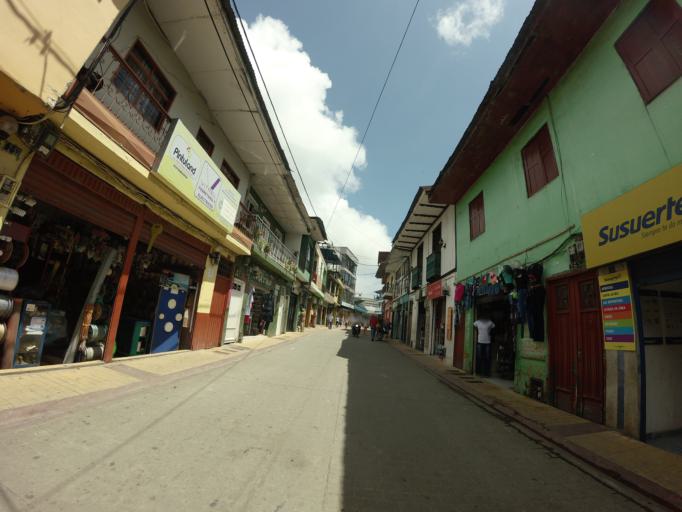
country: CO
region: Caldas
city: Marquetalia
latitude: 5.2964
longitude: -75.0545
